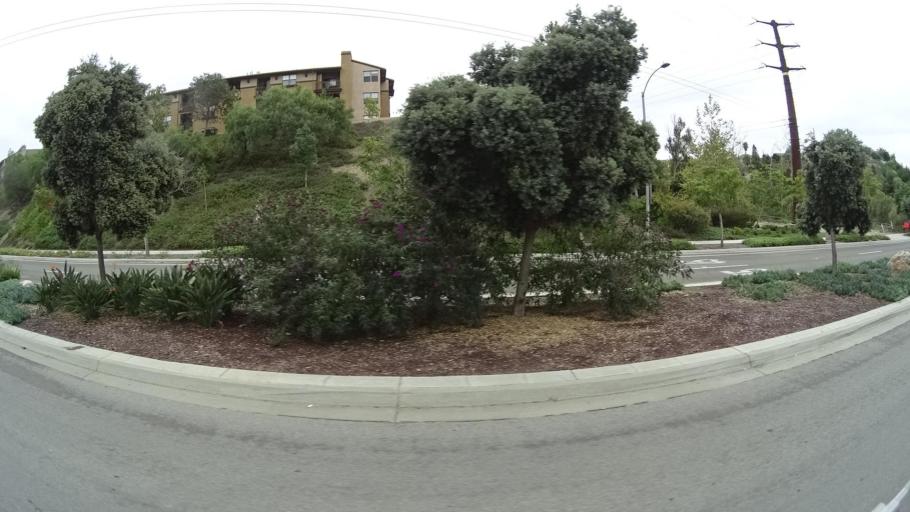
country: US
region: California
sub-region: San Diego County
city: Fairbanks Ranch
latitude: 33.0206
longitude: -117.1195
